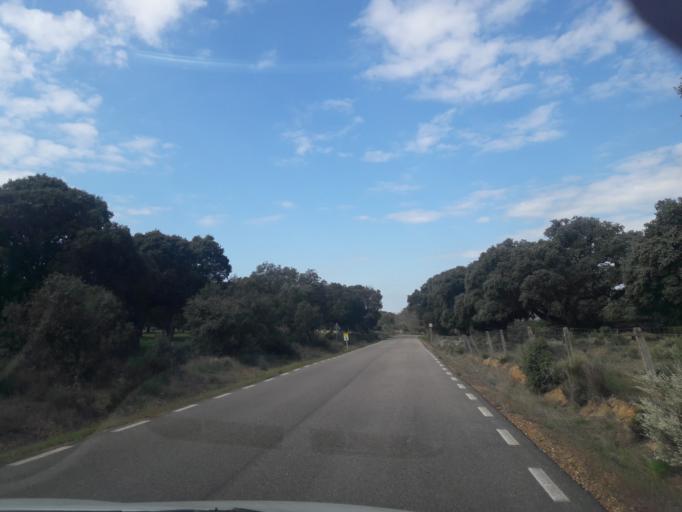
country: ES
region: Castille and Leon
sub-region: Provincia de Salamanca
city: Zamarra
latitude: 40.5611
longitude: -6.4599
